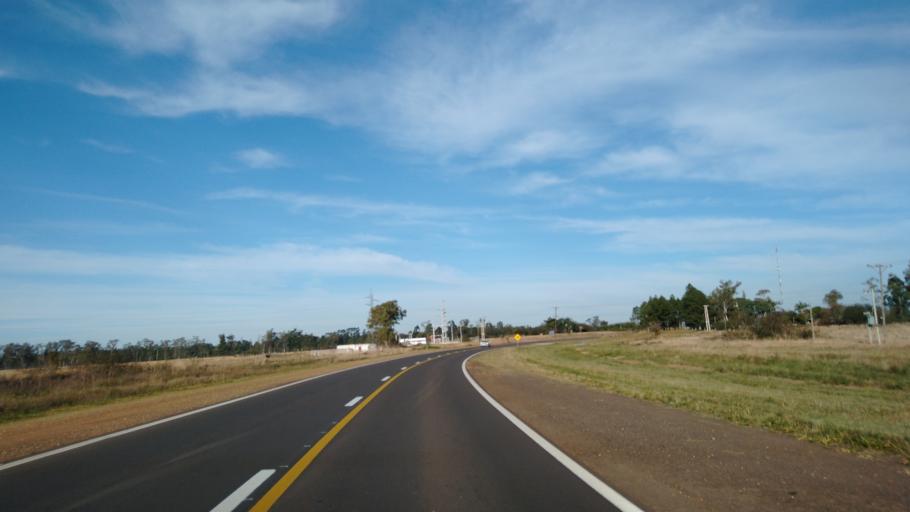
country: AR
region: Corrientes
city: Yapeyu
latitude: -29.4185
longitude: -56.8380
